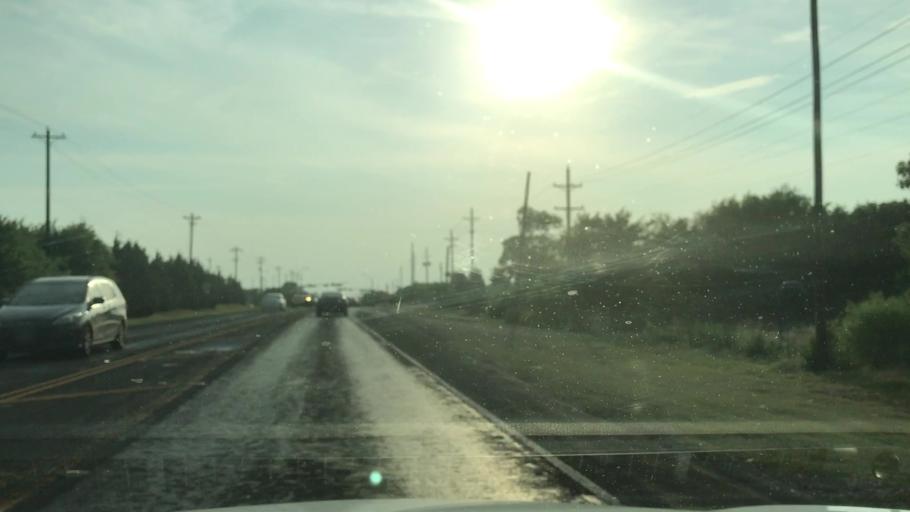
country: US
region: Texas
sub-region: Rockwall County
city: Rockwall
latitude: 32.9067
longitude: -96.4283
